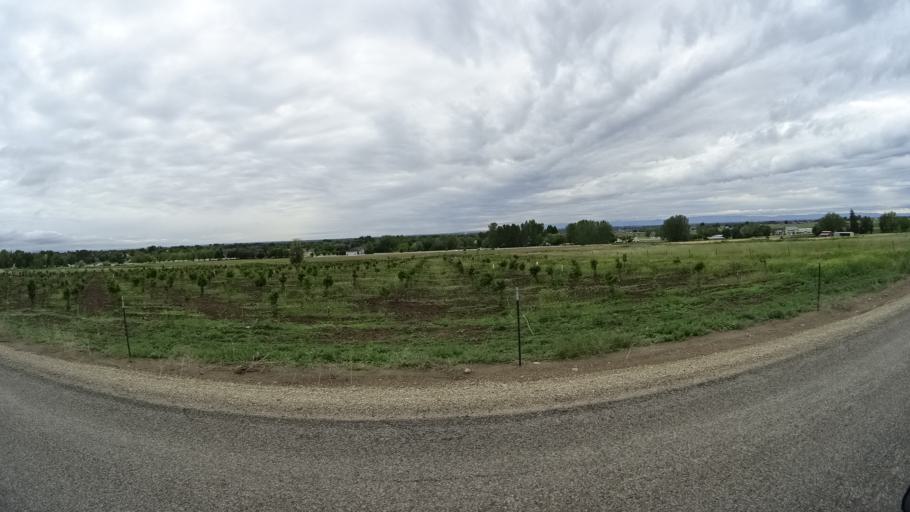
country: US
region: Idaho
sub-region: Ada County
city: Eagle
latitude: 43.7357
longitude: -116.4080
